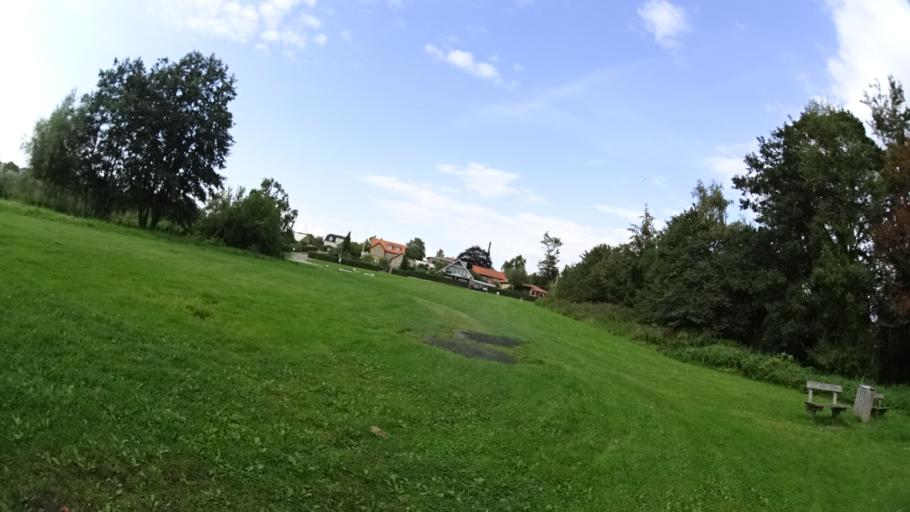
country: DK
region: Central Jutland
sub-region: Arhus Kommune
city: Stavtrup
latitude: 56.1501
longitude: 10.0982
